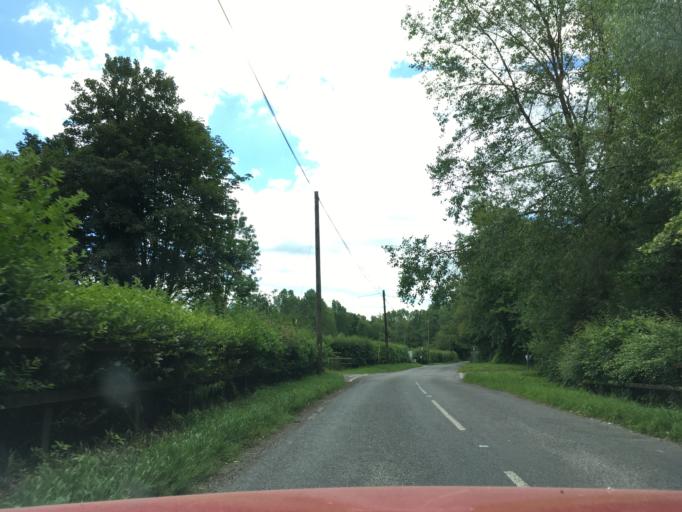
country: GB
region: England
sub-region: West Berkshire
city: Welford
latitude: 51.4573
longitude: -1.4110
